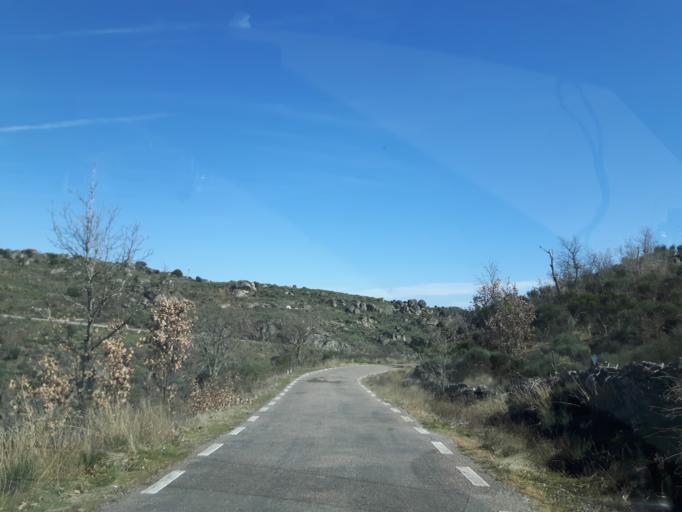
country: ES
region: Castille and Leon
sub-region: Provincia de Salamanca
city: Saldeana
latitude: 40.9982
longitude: -6.6299
